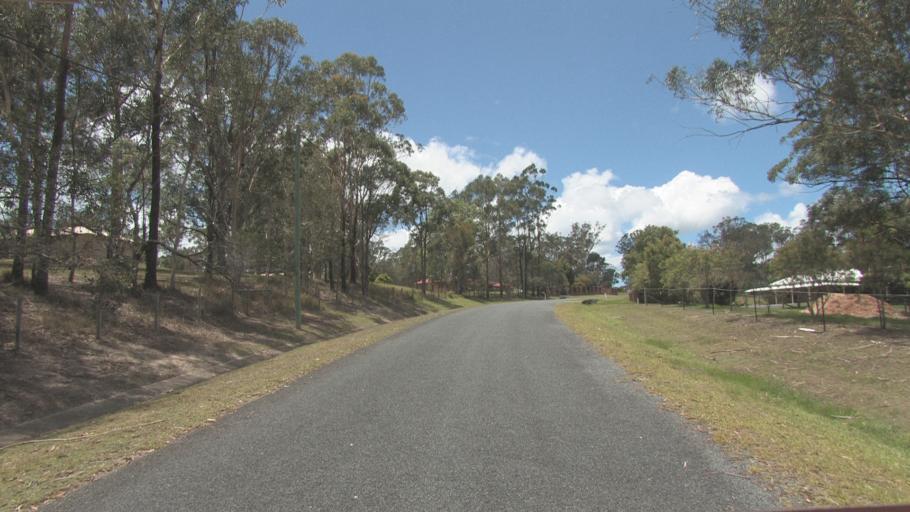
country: AU
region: Queensland
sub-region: Redland
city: Redland Bay
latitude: -27.6589
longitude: 153.2679
